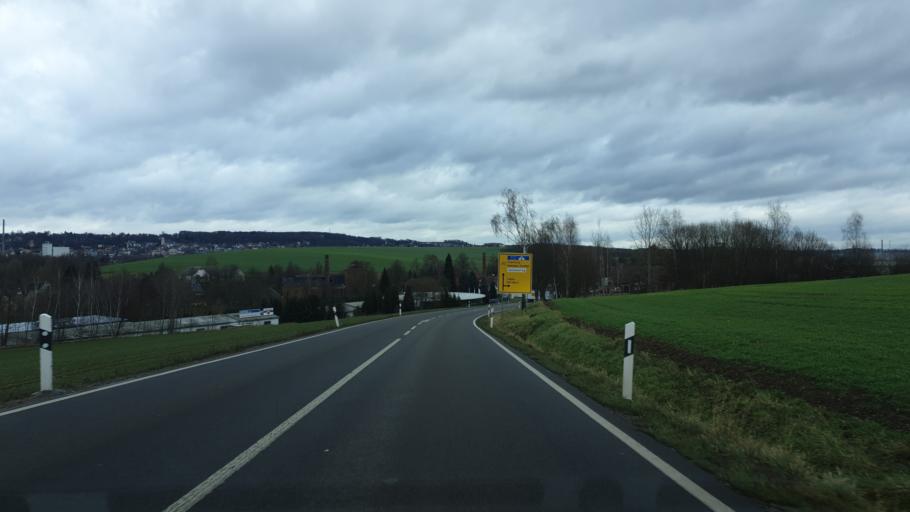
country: DE
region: Saxony
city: Oberlungwitz
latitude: 50.7786
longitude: 12.6928
